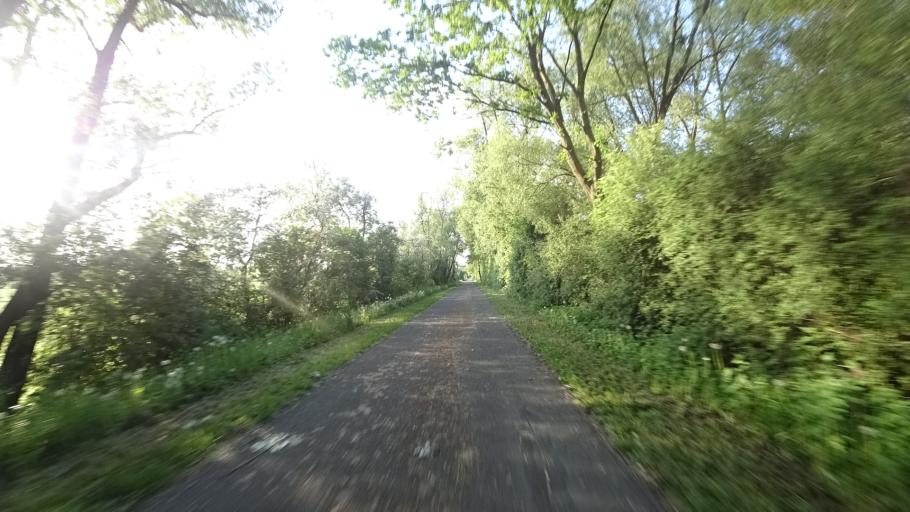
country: BE
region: Wallonia
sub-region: Province de Namur
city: Eghezee
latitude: 50.6011
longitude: 4.9097
